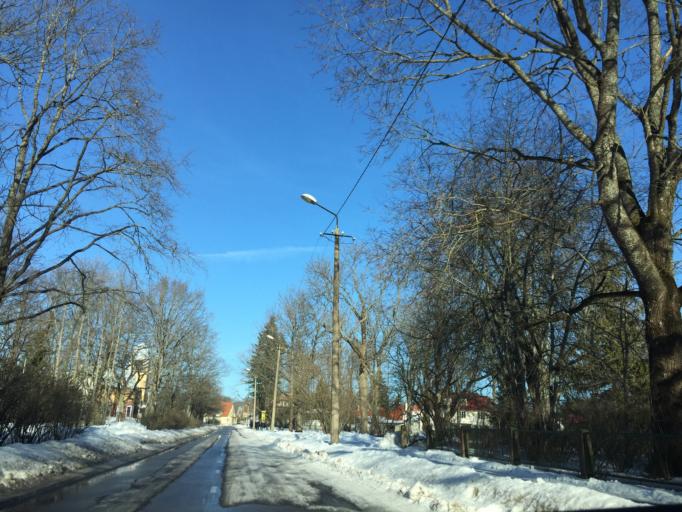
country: EE
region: Paernumaa
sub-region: Paernu linn
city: Parnu
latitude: 58.3788
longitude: 24.4927
